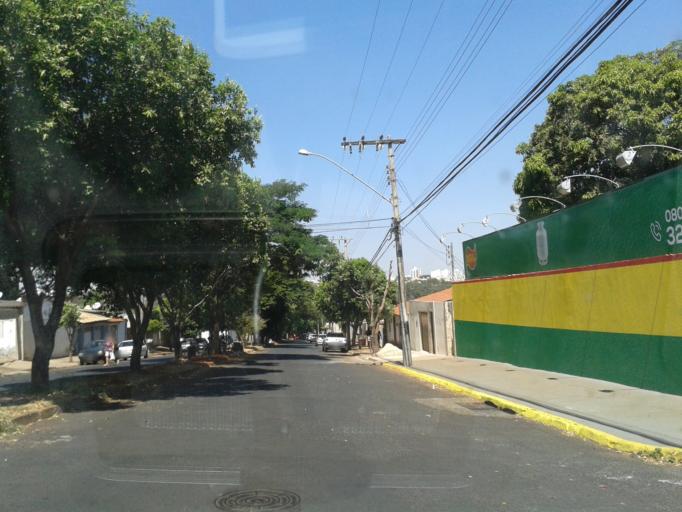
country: BR
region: Minas Gerais
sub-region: Uberlandia
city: Uberlandia
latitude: -18.9060
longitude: -48.2426
